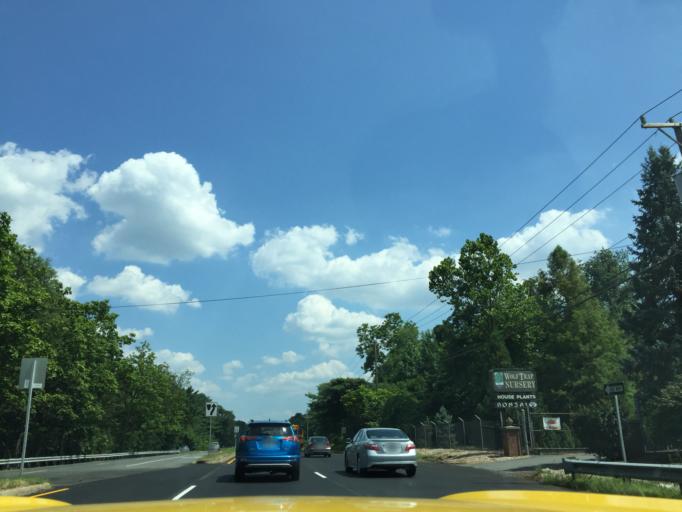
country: US
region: Virginia
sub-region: Fairfax County
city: Wolf Trap
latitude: 38.9563
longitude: -77.2723
